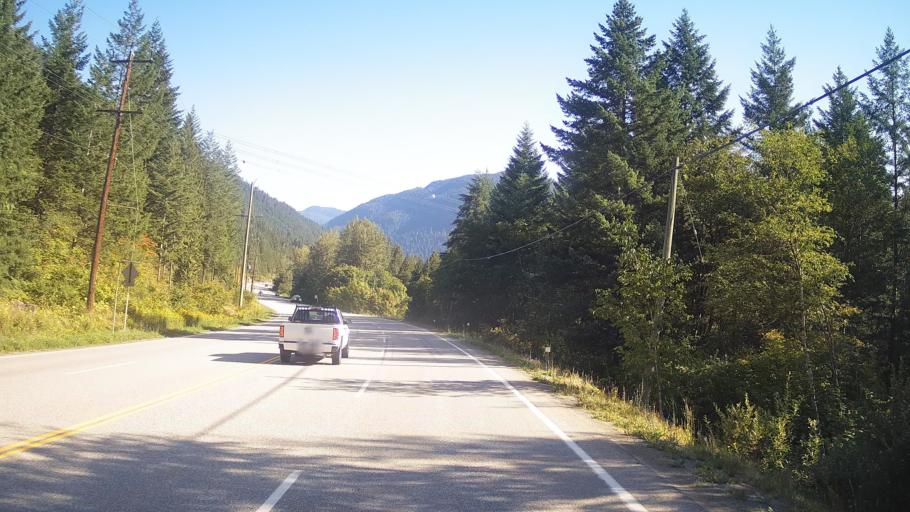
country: CA
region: British Columbia
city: Hope
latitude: 49.6710
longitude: -121.4186
